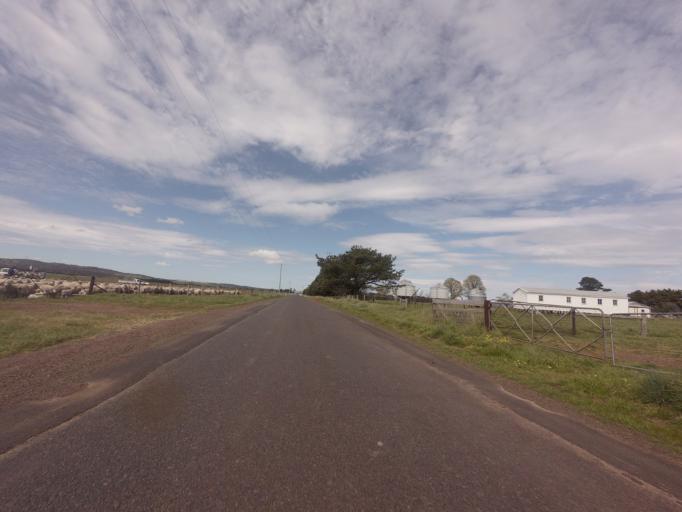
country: AU
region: Tasmania
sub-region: Northern Midlands
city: Evandale
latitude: -41.8117
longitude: 147.2891
